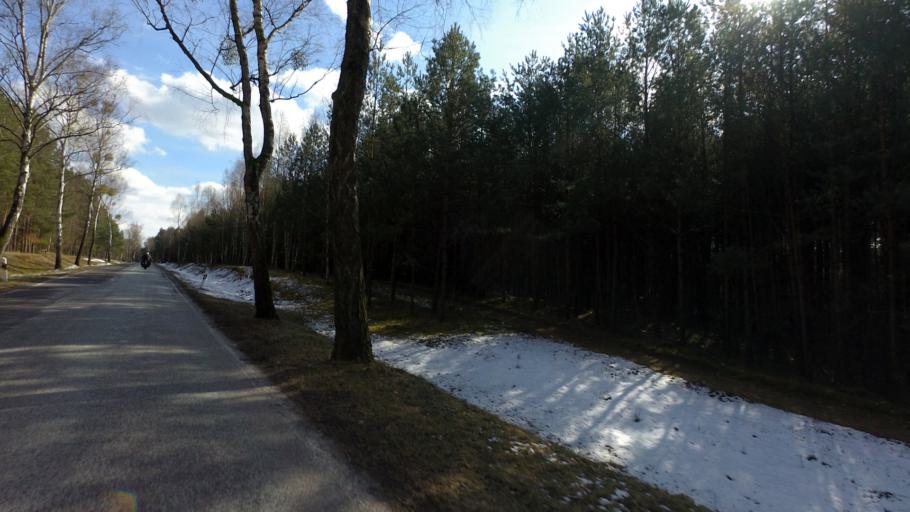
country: DE
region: Brandenburg
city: Biesenthal
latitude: 52.7856
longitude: 13.6083
